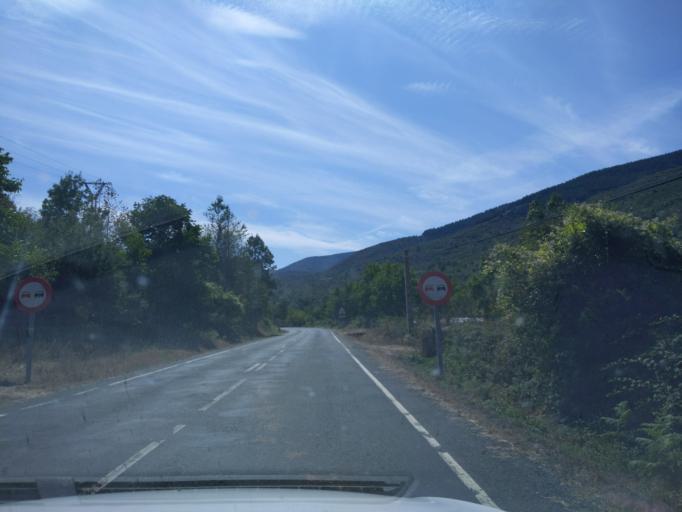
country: ES
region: La Rioja
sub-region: Provincia de La Rioja
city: Ezcaray
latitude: 42.3018
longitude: -3.0242
